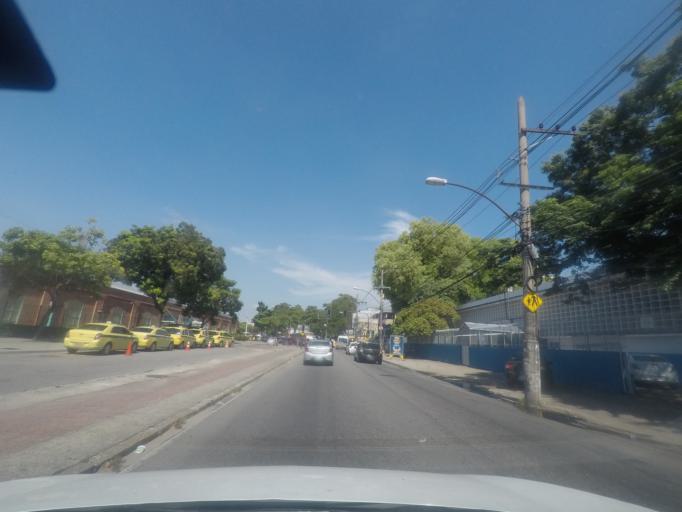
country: BR
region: Rio de Janeiro
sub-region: Nilopolis
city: Nilopolis
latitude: -22.8801
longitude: -43.4676
